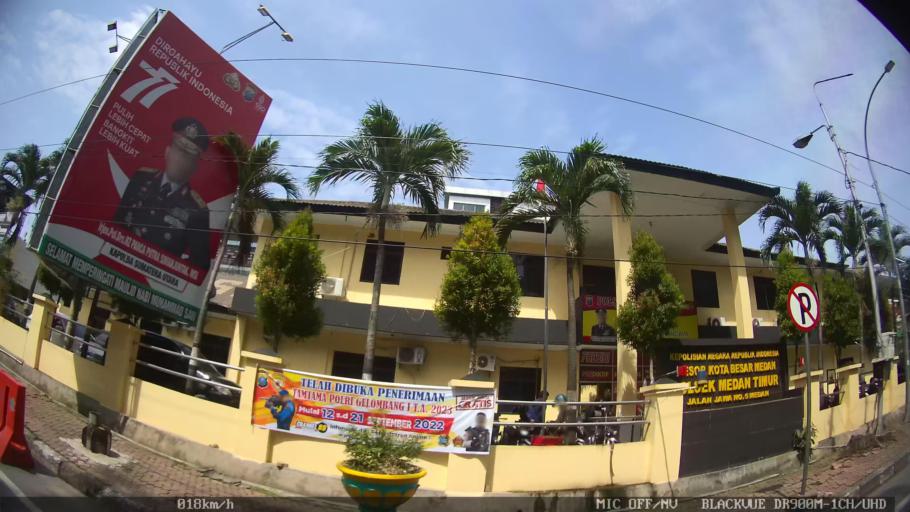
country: ID
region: North Sumatra
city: Medan
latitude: 3.5903
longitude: 98.6809
